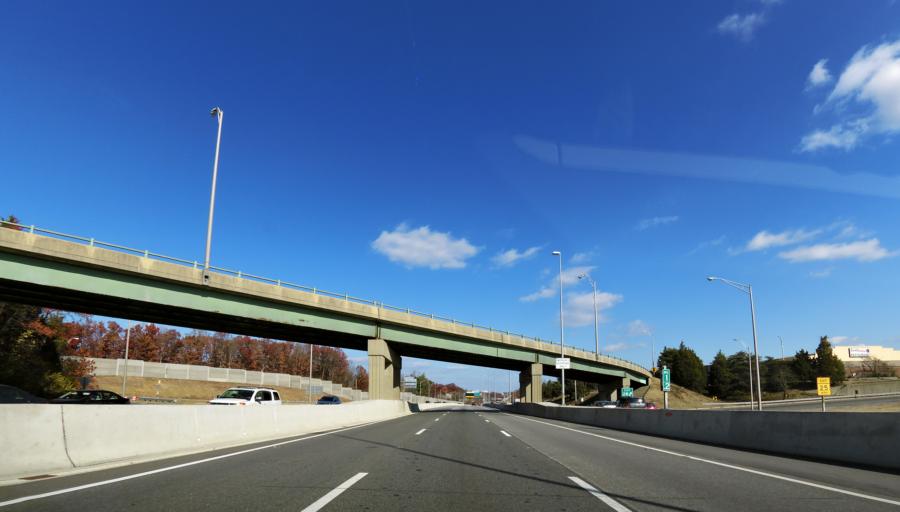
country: US
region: Virginia
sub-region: Fairfax County
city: Lincolnia
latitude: 38.8026
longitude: -77.1630
